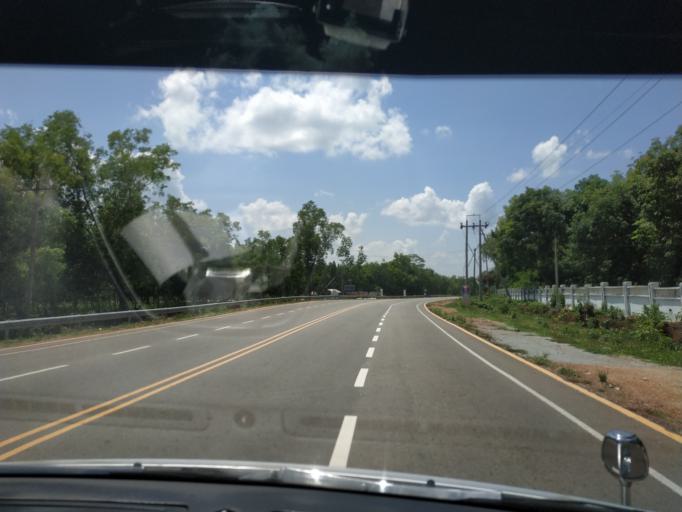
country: MM
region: Mon
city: Kyaikto
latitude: 17.3396
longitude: 97.0385
